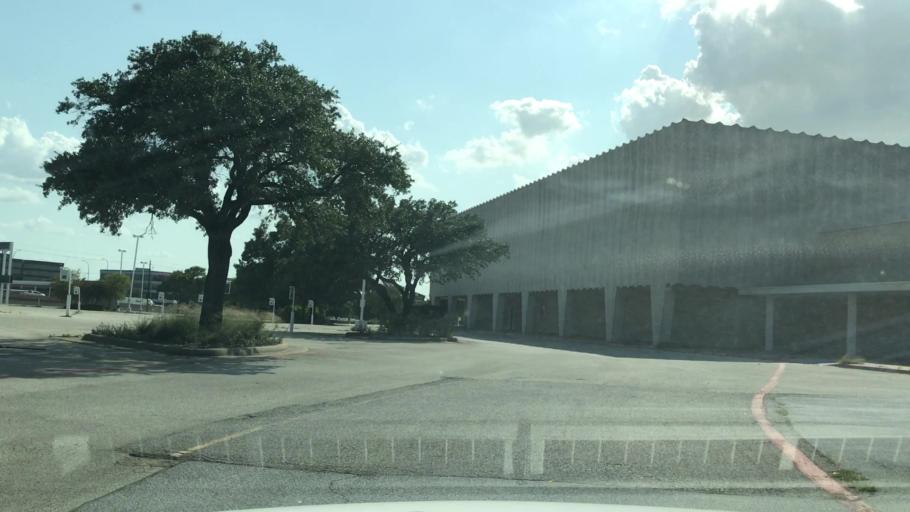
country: US
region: Texas
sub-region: Dallas County
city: Addison
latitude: 32.9281
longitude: -96.8059
